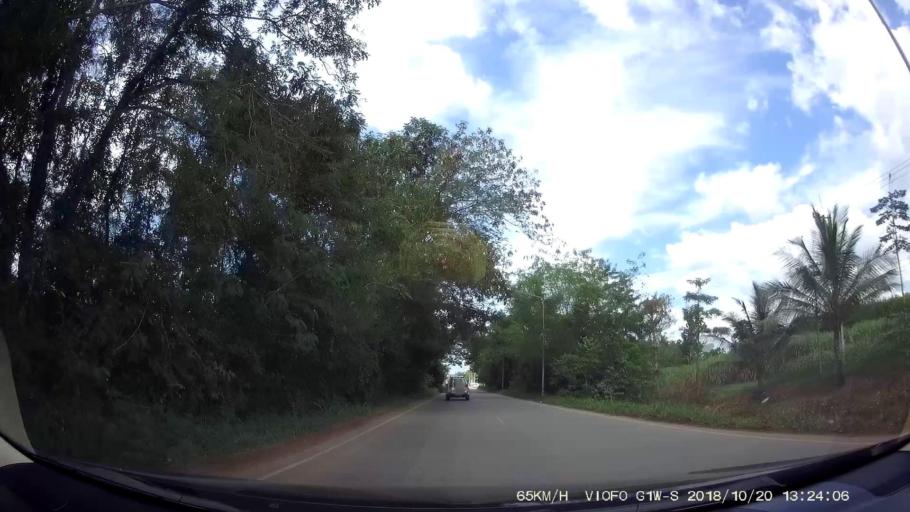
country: TH
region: Chaiyaphum
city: Khon San
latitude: 16.5907
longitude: 101.9250
